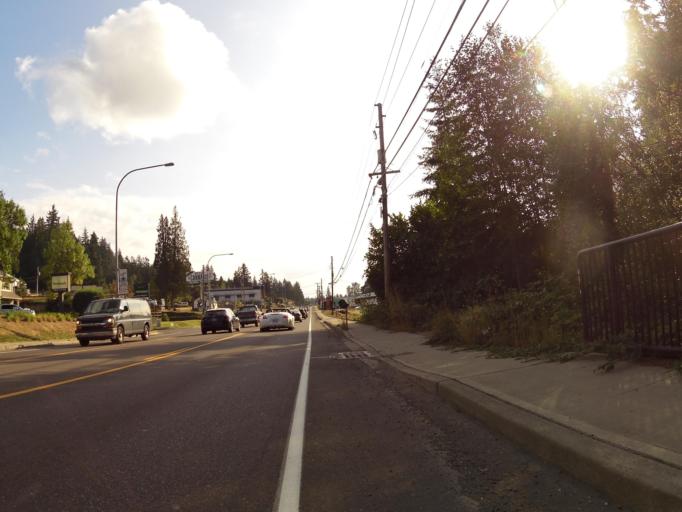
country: US
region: Washington
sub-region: Mason County
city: Belfair
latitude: 47.4490
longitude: -122.8288
